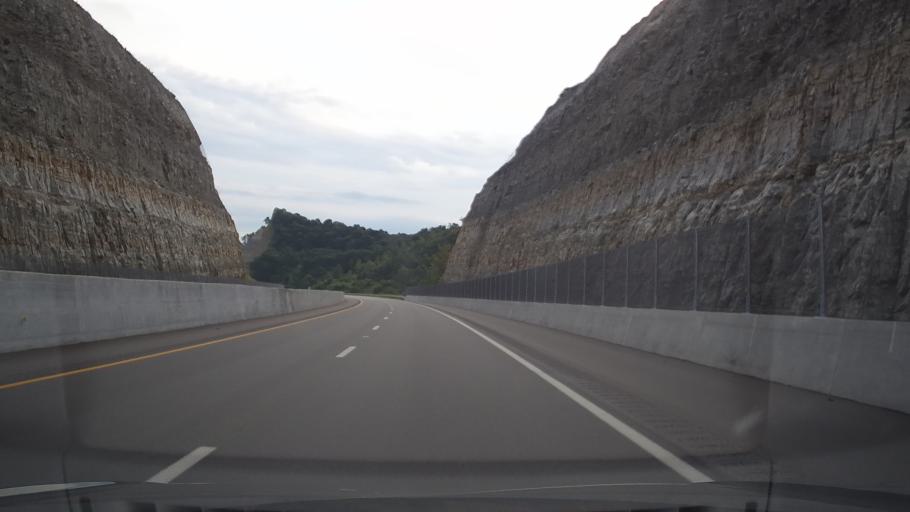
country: US
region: Ohio
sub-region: Scioto County
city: Lucasville
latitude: 38.8981
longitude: -82.9676
